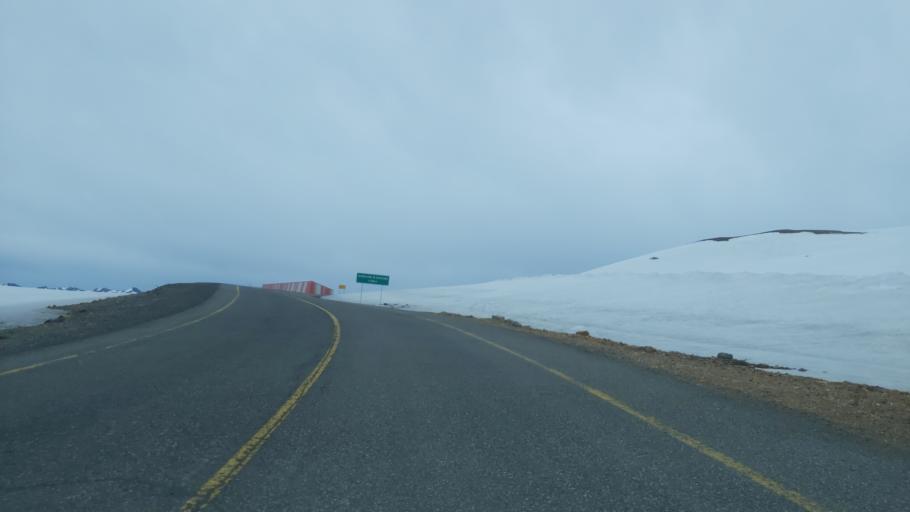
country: CL
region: Maule
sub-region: Provincia de Linares
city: Colbun
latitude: -36.0072
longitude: -70.4798
